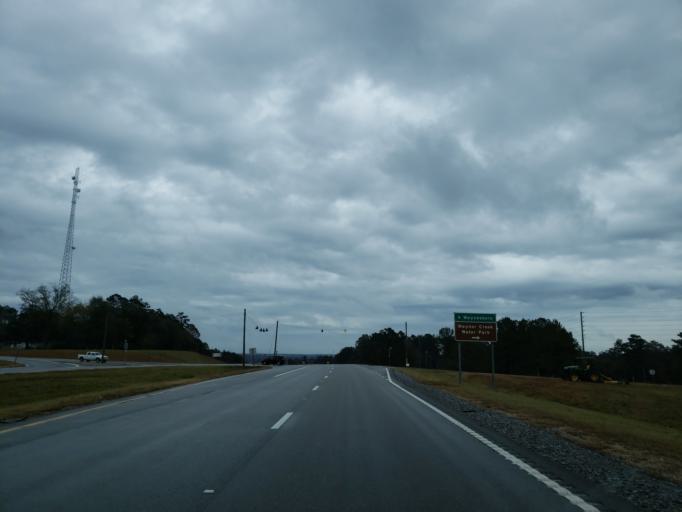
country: US
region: Mississippi
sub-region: Wayne County
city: Waynesboro
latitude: 31.6832
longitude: -88.6943
